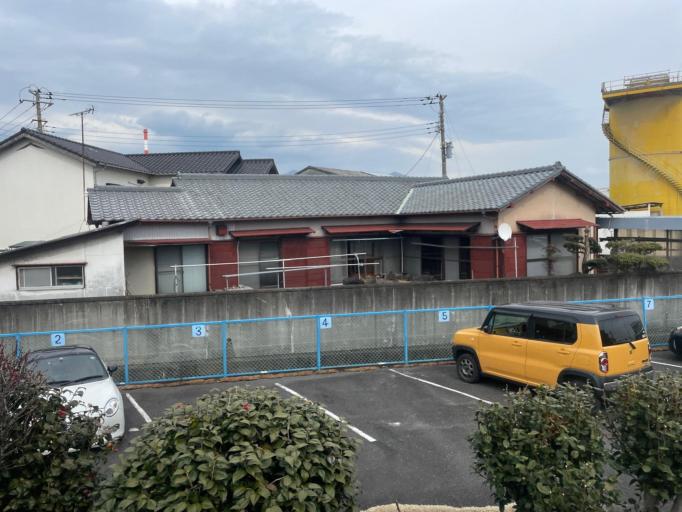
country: JP
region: Shizuoka
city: Fuji
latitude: 35.1587
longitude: 138.6893
